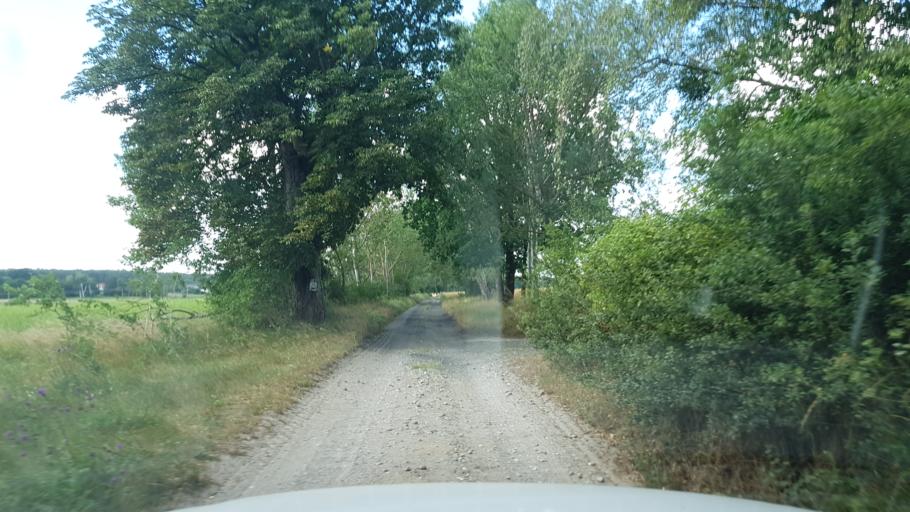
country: PL
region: West Pomeranian Voivodeship
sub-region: Powiat mysliborski
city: Debno
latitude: 52.7203
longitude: 14.6565
